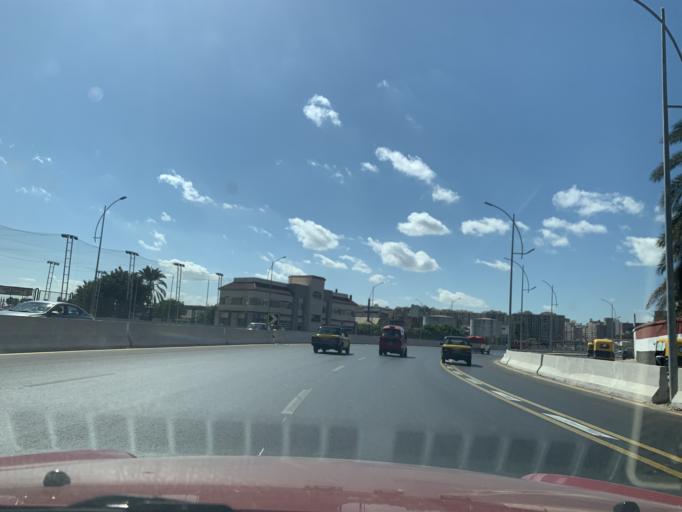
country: EG
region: Alexandria
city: Alexandria
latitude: 31.1913
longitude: 29.9302
